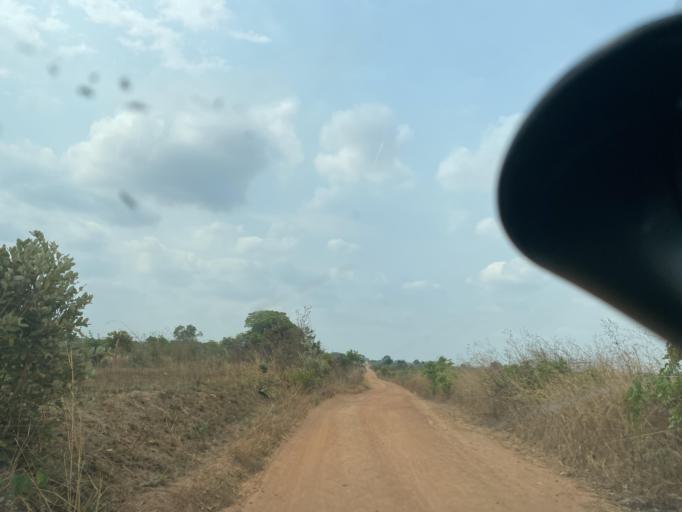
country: ZM
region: Lusaka
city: Lusaka
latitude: -15.1448
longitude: 28.3661
